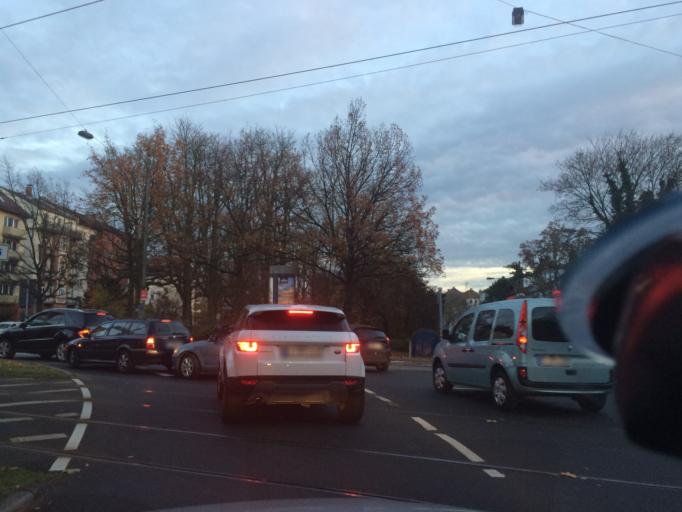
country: DE
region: Hesse
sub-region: Regierungsbezirk Darmstadt
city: Frankfurt am Main
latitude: 50.1203
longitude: 8.7046
